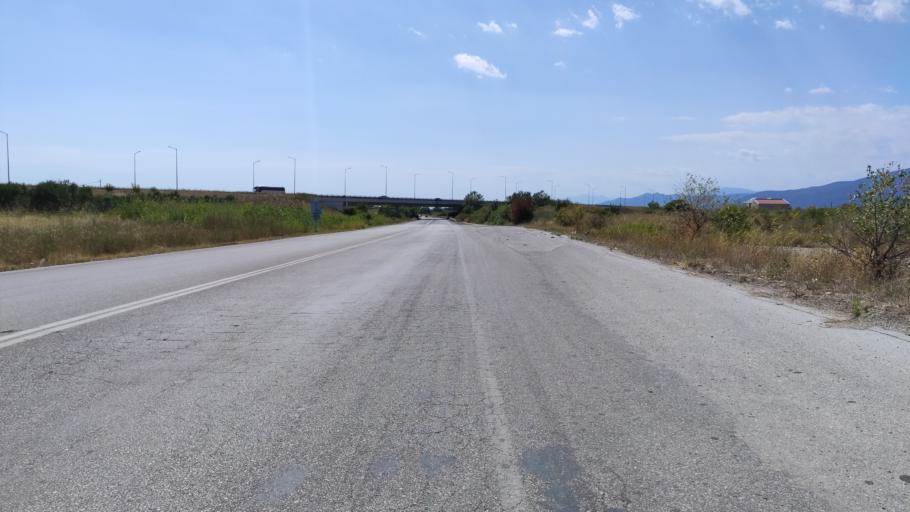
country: GR
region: East Macedonia and Thrace
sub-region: Nomos Rodopis
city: Komotini
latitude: 41.1085
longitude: 25.3464
